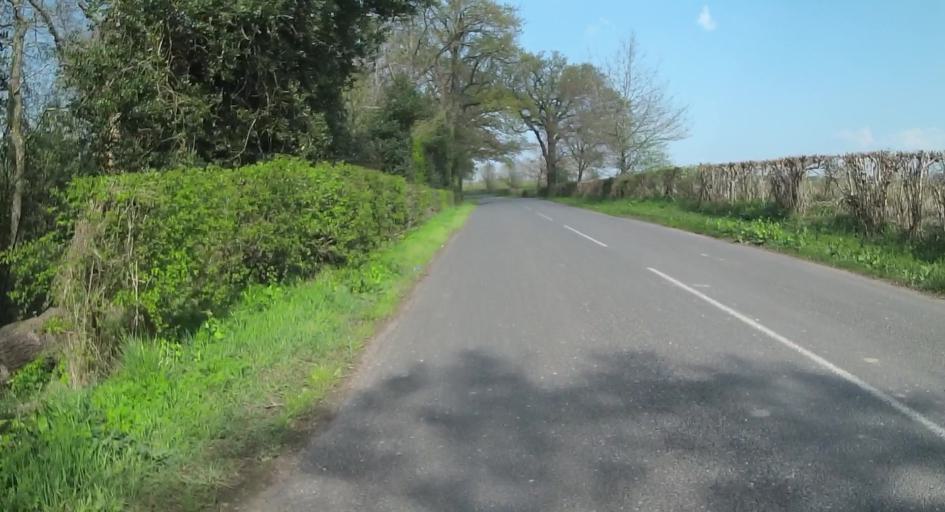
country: GB
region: England
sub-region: Hampshire
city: Basingstoke
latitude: 51.3112
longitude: -1.0843
